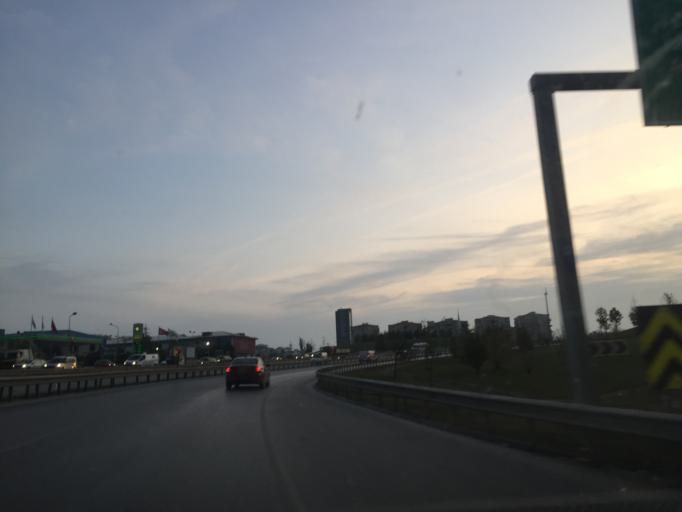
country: TR
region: Istanbul
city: Samandira
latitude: 40.9709
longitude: 29.2199
